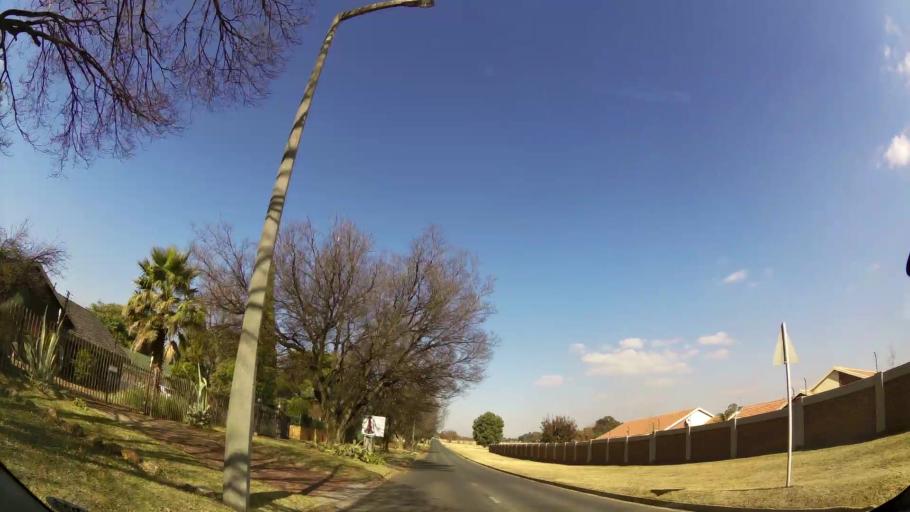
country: ZA
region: Gauteng
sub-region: Ekurhuleni Metropolitan Municipality
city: Benoni
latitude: -26.1405
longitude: 28.3381
